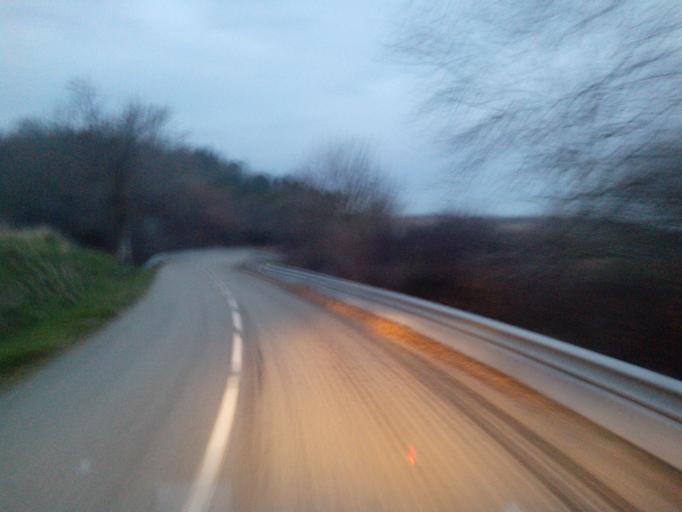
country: FR
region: Languedoc-Roussillon
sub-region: Departement de l'Aude
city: Belpech
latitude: 43.2770
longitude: 1.7873
